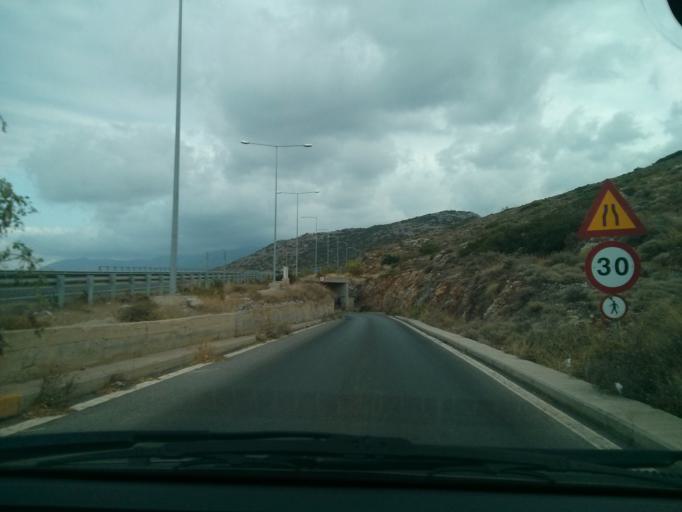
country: GR
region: Crete
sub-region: Nomos Irakleiou
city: Limin Khersonisou
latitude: 35.3006
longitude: 25.3989
